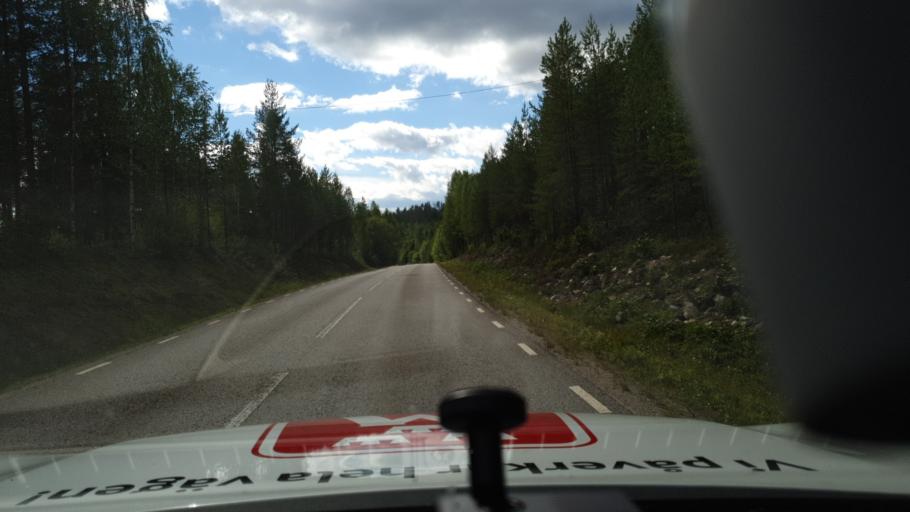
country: NO
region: Hedmark
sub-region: Trysil
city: Innbygda
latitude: 61.0260
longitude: 12.5577
